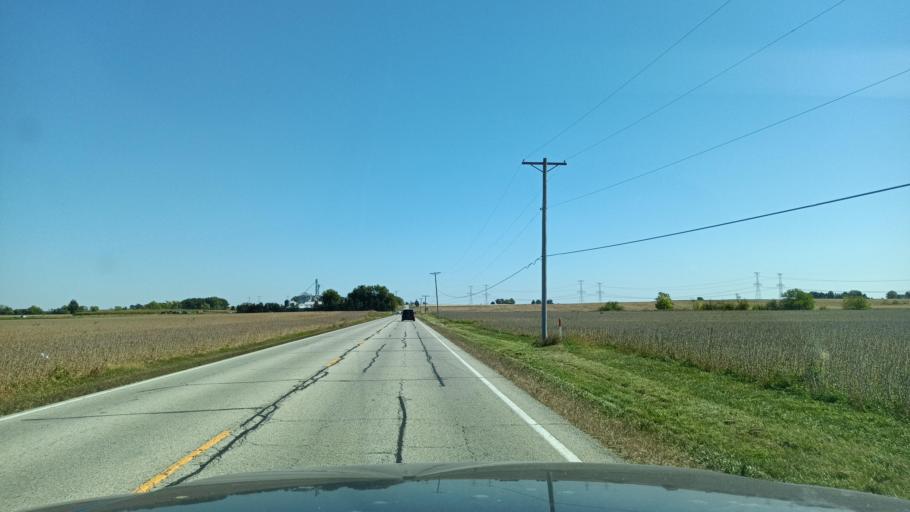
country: US
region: Illinois
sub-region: Tazewell County
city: Morton
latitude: 40.6135
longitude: -89.4268
